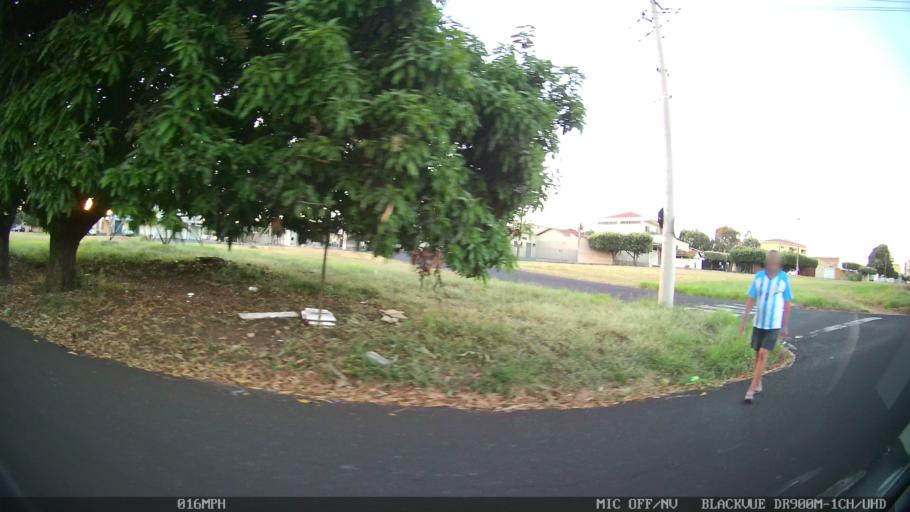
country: BR
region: Sao Paulo
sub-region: Sao Jose Do Rio Preto
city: Sao Jose do Rio Preto
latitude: -20.8432
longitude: -49.3760
